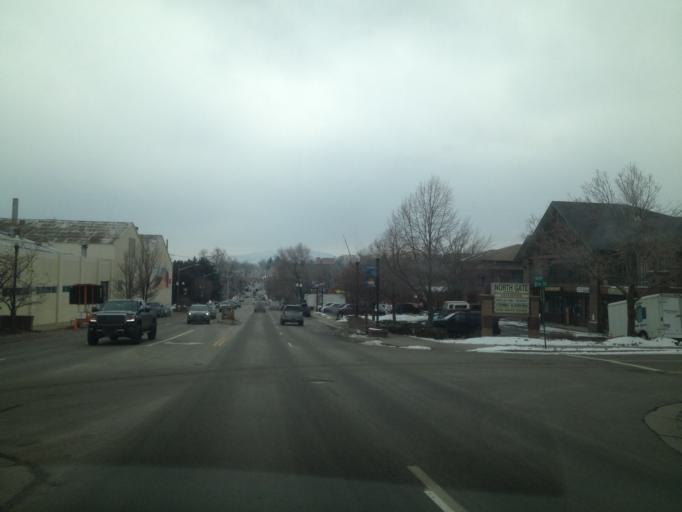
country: US
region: Colorado
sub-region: Jefferson County
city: Golden
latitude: 39.7593
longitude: -105.2250
